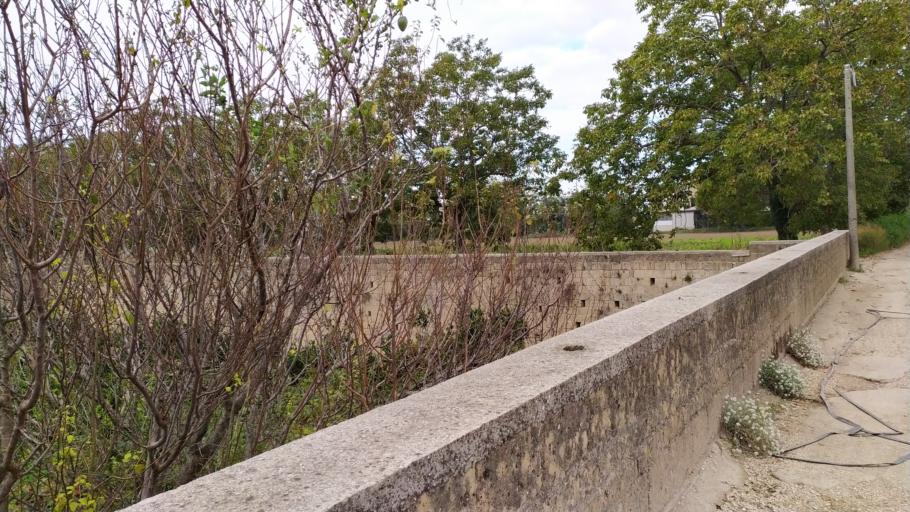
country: IT
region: Campania
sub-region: Provincia di Caserta
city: Montedecoro
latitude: 41.0166
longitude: 14.4059
